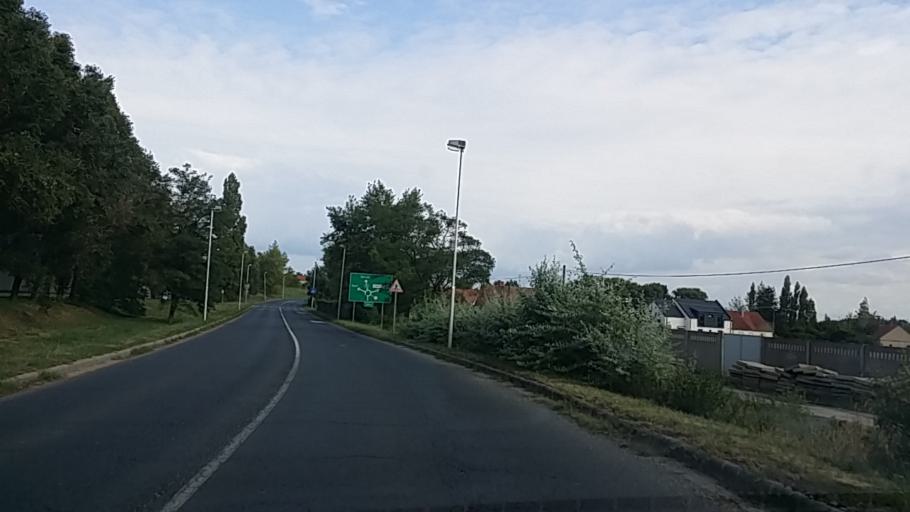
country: HU
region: Gyor-Moson-Sopron
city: Sopron
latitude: 47.6846
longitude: 16.6092
